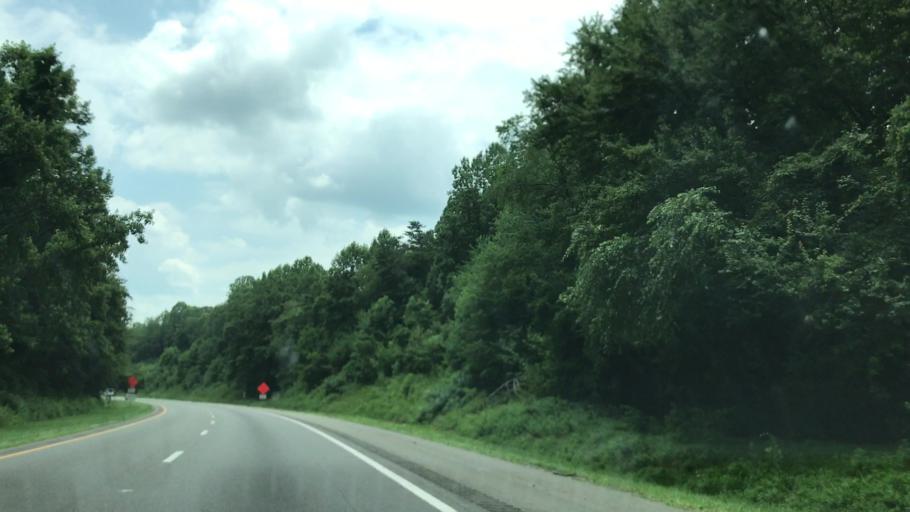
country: US
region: North Carolina
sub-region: Surry County
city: Dobson
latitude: 36.4390
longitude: -80.7787
